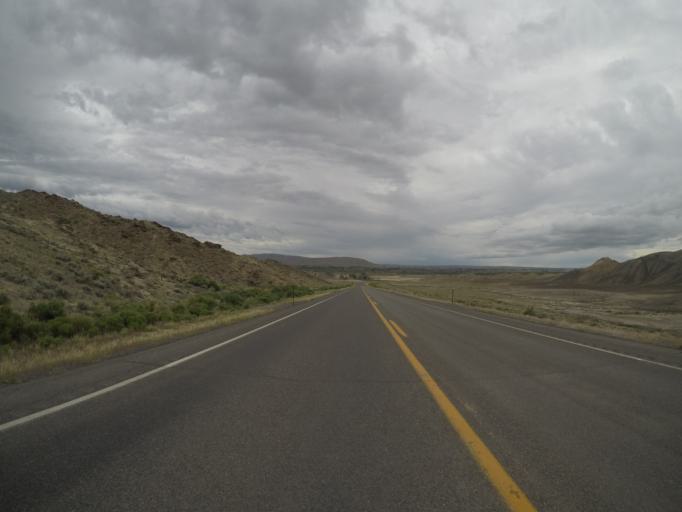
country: US
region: Wyoming
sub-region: Big Horn County
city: Lovell
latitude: 44.8849
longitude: -108.2891
